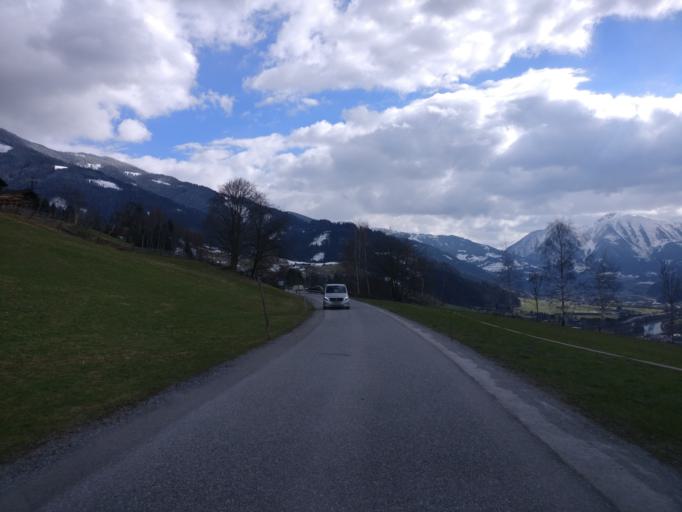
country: AT
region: Salzburg
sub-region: Politischer Bezirk Sankt Johann im Pongau
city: Bischofshofen
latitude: 47.4095
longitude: 13.2282
